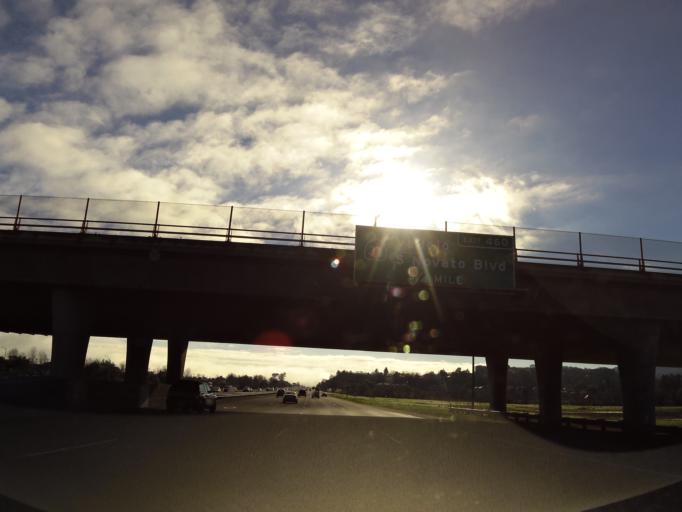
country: US
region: California
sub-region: Marin County
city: Novato
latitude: 38.0925
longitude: -122.5596
